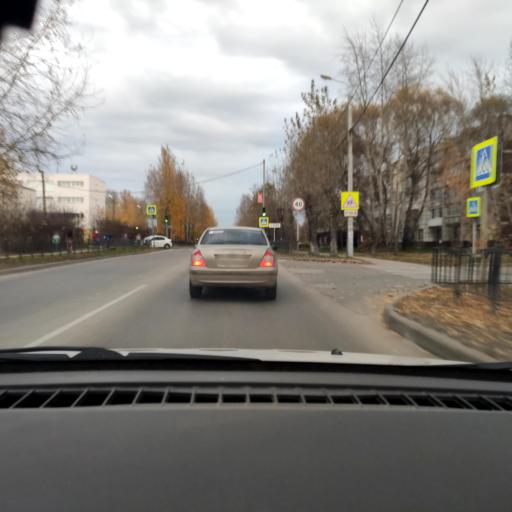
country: RU
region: Perm
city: Perm
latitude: 58.1067
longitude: 56.3814
